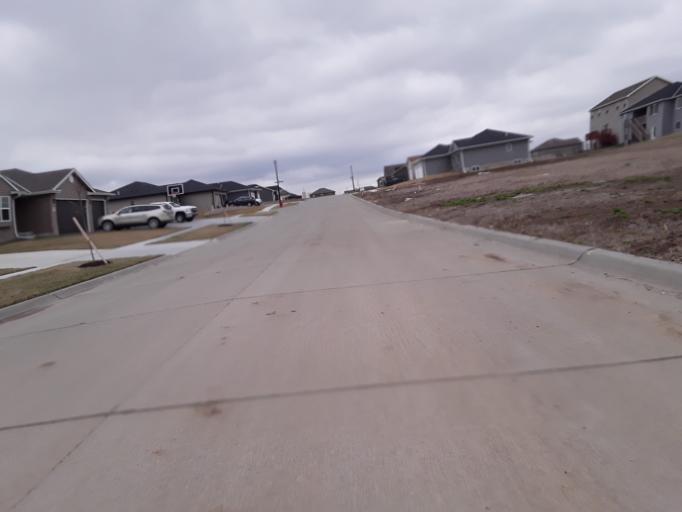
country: US
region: Nebraska
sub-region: Lancaster County
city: Lincoln
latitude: 40.8457
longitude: -96.5944
